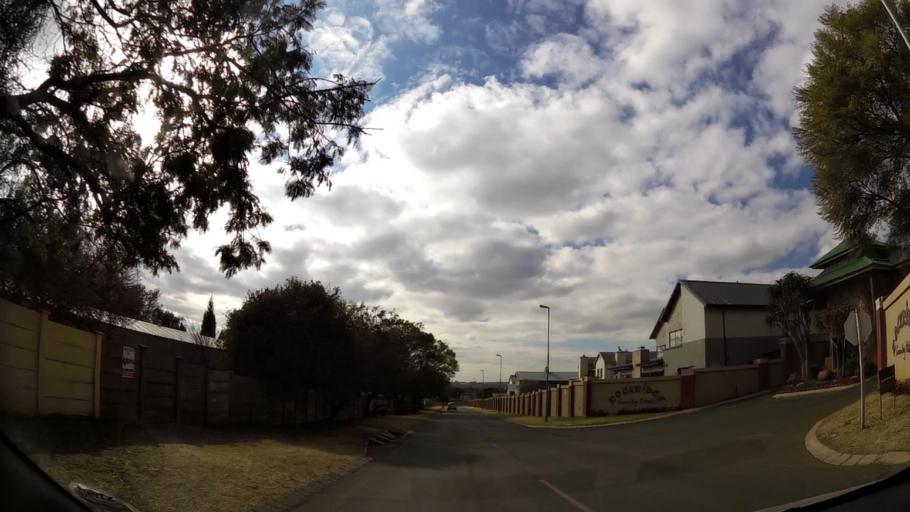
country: ZA
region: Gauteng
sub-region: City of Johannesburg Metropolitan Municipality
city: Roodepoort
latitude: -26.1028
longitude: 27.8756
